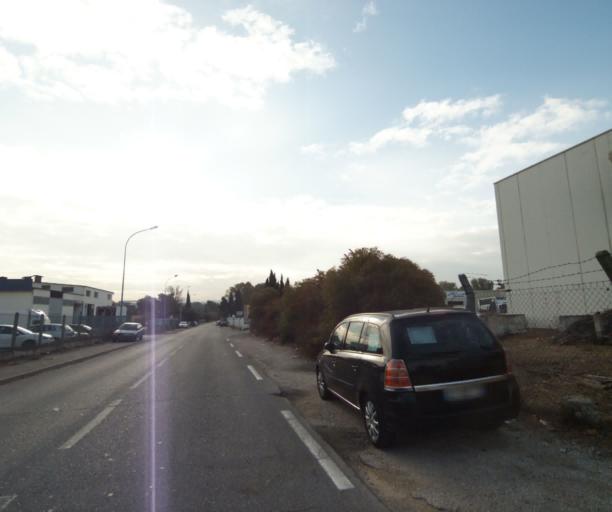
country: FR
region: Provence-Alpes-Cote d'Azur
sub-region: Departement des Bouches-du-Rhone
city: Saint-Victoret
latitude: 43.4230
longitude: 5.2414
